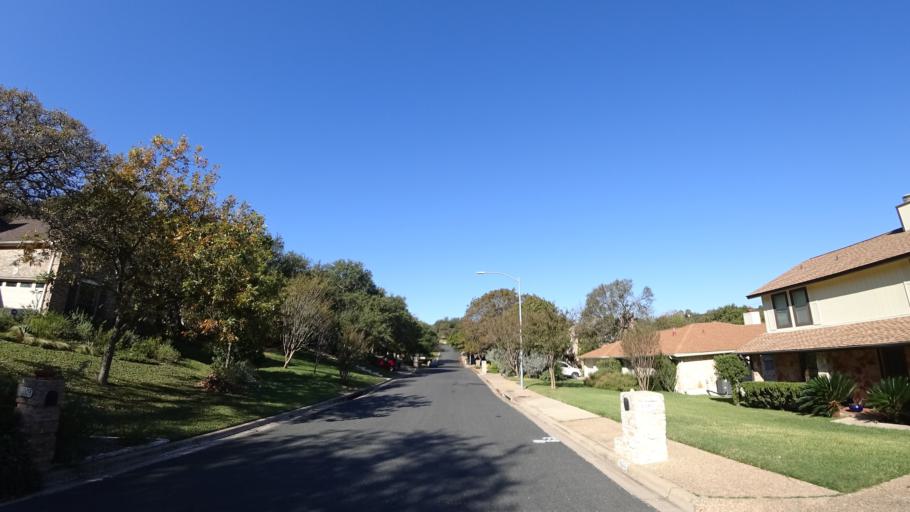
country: US
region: Texas
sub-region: Williamson County
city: Jollyville
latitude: 30.4104
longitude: -97.7644
